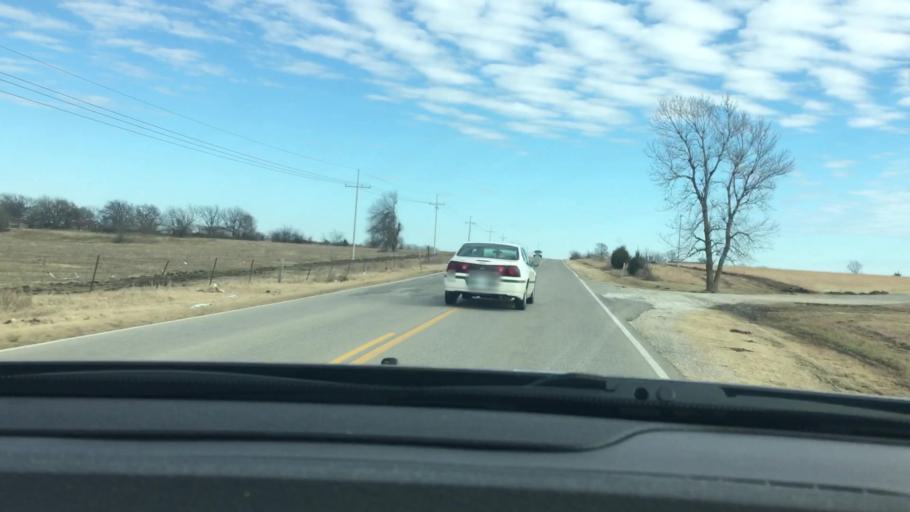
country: US
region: Oklahoma
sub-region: Garvin County
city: Stratford
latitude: 34.7967
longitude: -96.9191
